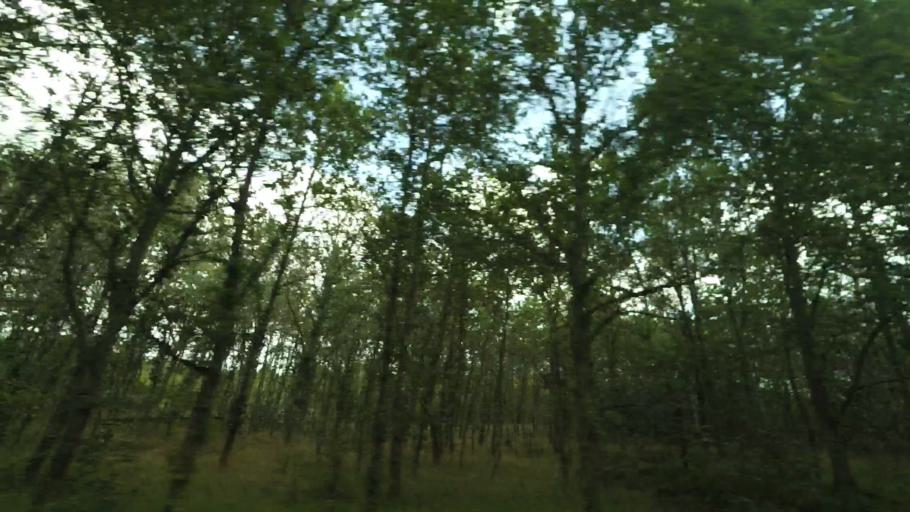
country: DK
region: Central Jutland
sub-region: Norddjurs Kommune
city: Auning
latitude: 56.5109
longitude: 10.4142
